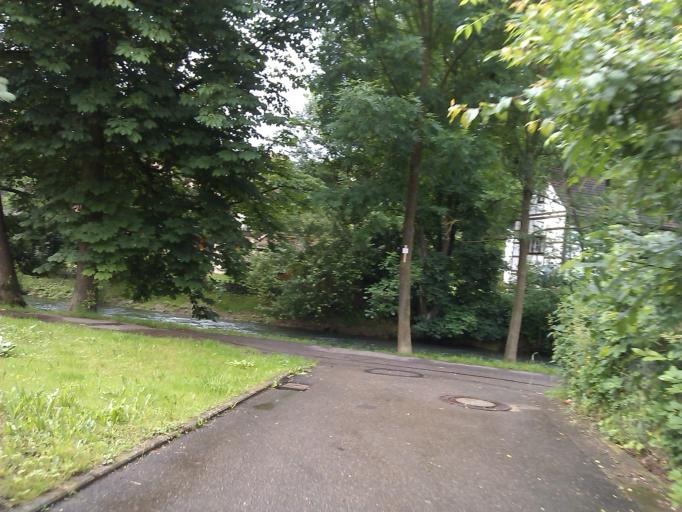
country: DE
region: Baden-Wuerttemberg
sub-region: Regierungsbezirk Stuttgart
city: Giengen an der Brenz
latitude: 48.6184
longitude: 10.2467
